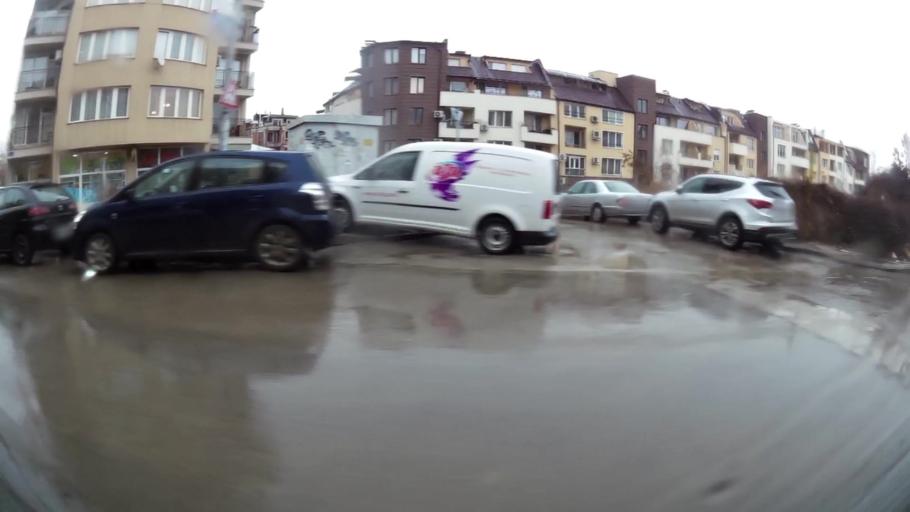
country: BG
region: Sofia-Capital
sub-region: Stolichna Obshtina
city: Sofia
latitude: 42.6573
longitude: 23.3637
